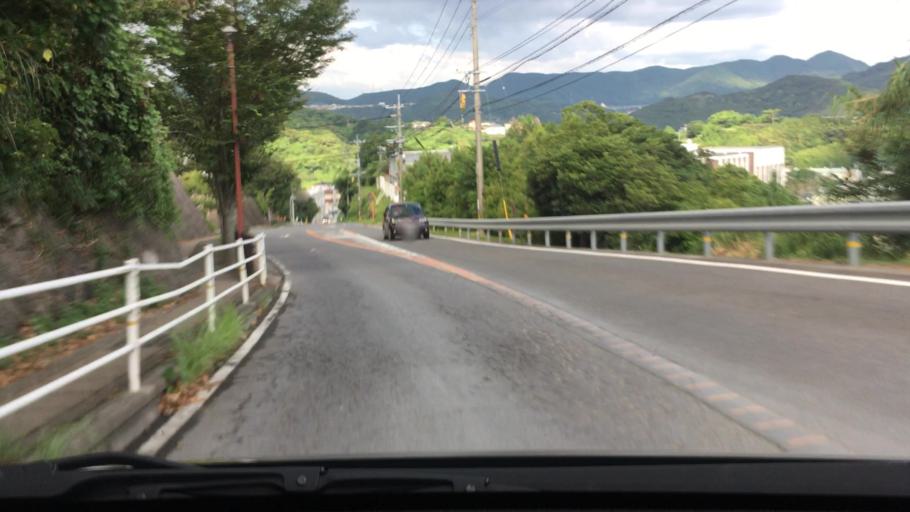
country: JP
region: Nagasaki
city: Togitsu
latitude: 32.8251
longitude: 129.7615
